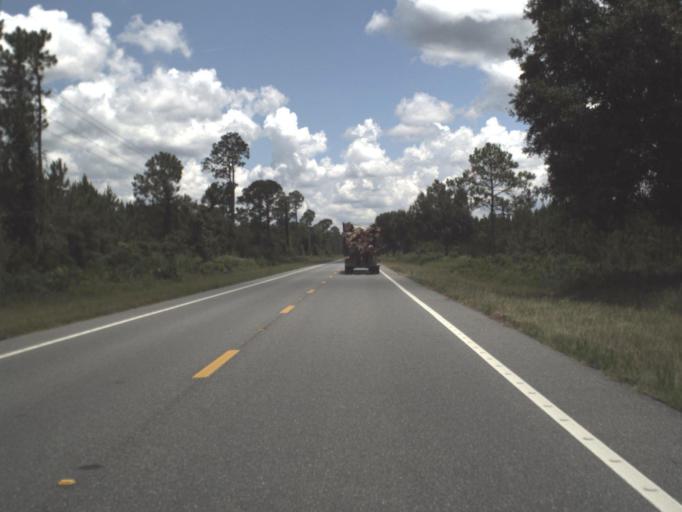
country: US
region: Florida
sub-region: Taylor County
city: Perry
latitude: 30.1428
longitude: -83.8315
